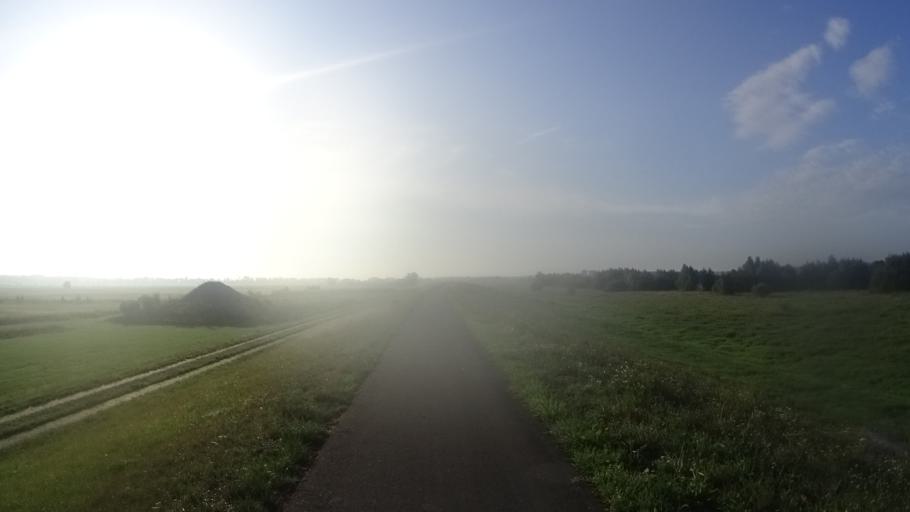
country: DE
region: Brandenburg
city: Lenzen
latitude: 53.0689
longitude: 11.4911
